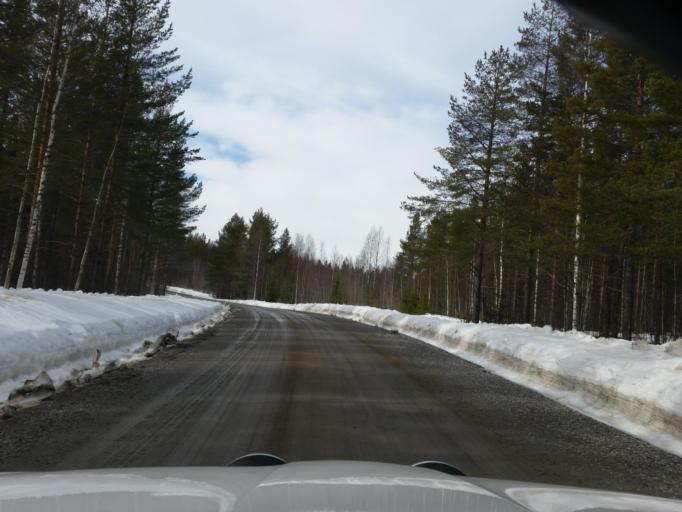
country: SE
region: Vaesterbotten
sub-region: Skelleftea Kommun
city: Storvik
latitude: 65.2191
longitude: 20.8859
